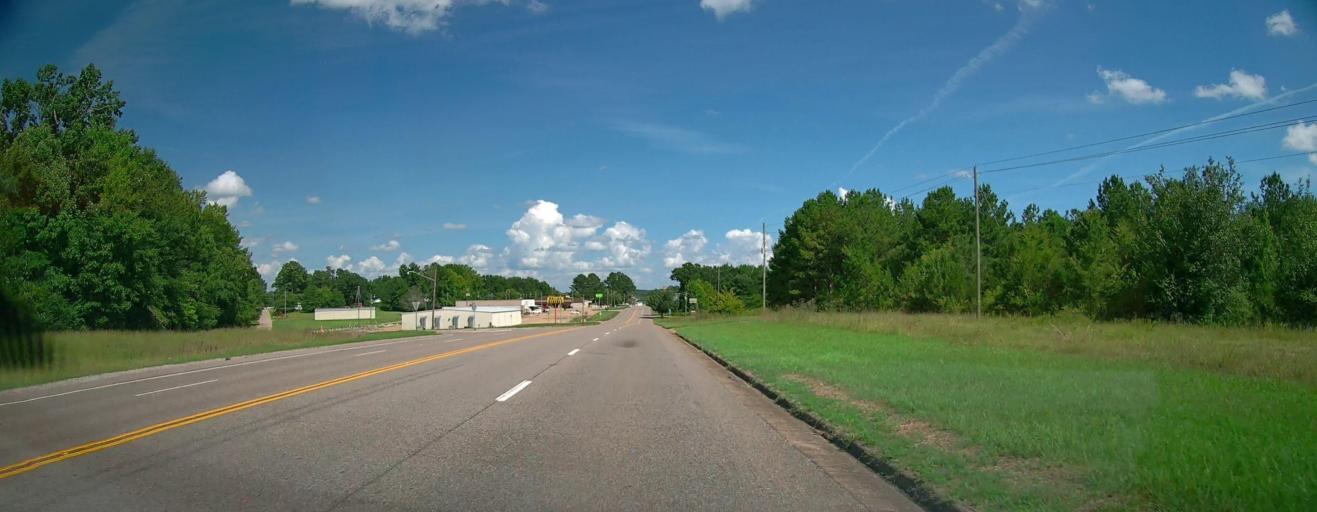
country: US
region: Alabama
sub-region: Pickens County
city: Reform
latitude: 33.3851
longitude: -88.0285
